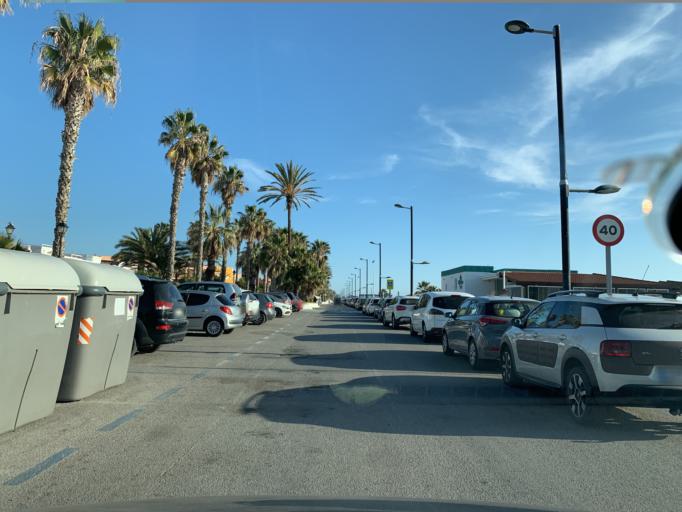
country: ES
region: Andalusia
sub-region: Provincia de Granada
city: Salobrena
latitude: 36.7355
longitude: -3.5908
